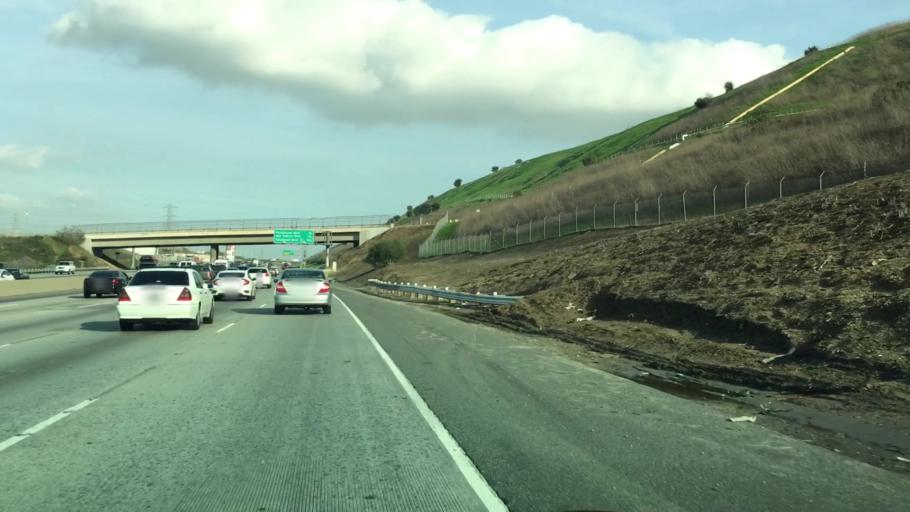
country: US
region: California
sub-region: Los Angeles County
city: Montebello
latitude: 34.0335
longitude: -118.1106
